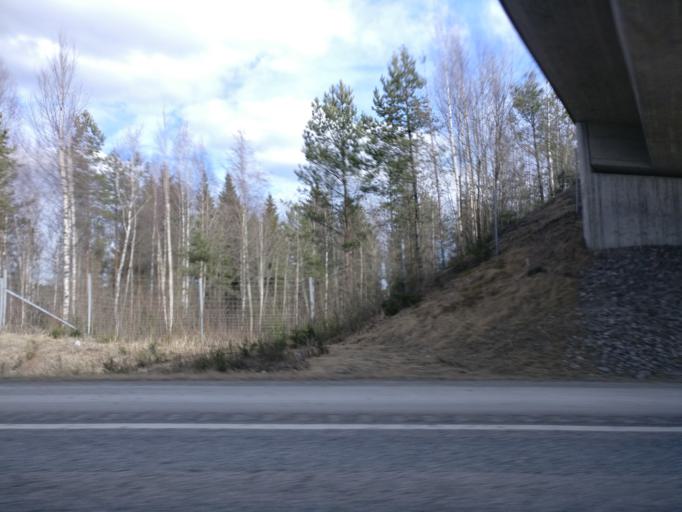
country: FI
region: Haeme
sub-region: Haemeenlinna
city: Haemeenlinna
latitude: 60.9565
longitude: 24.4875
